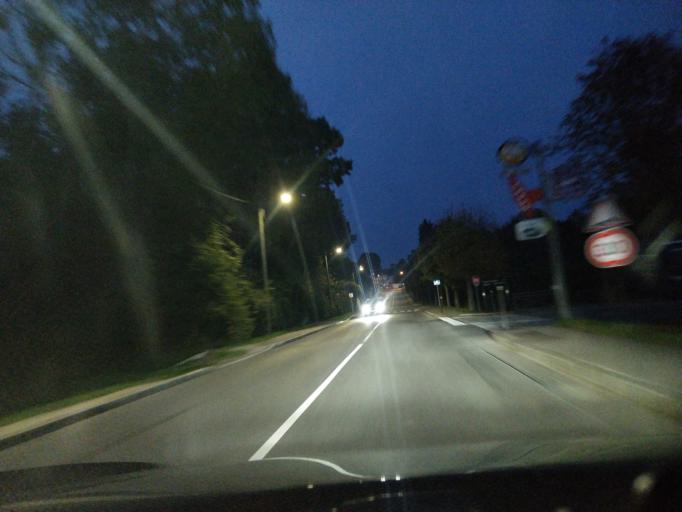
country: FR
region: Ile-de-France
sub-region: Departement de l'Essonne
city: Forges-les-Bains
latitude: 48.6292
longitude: 2.0950
